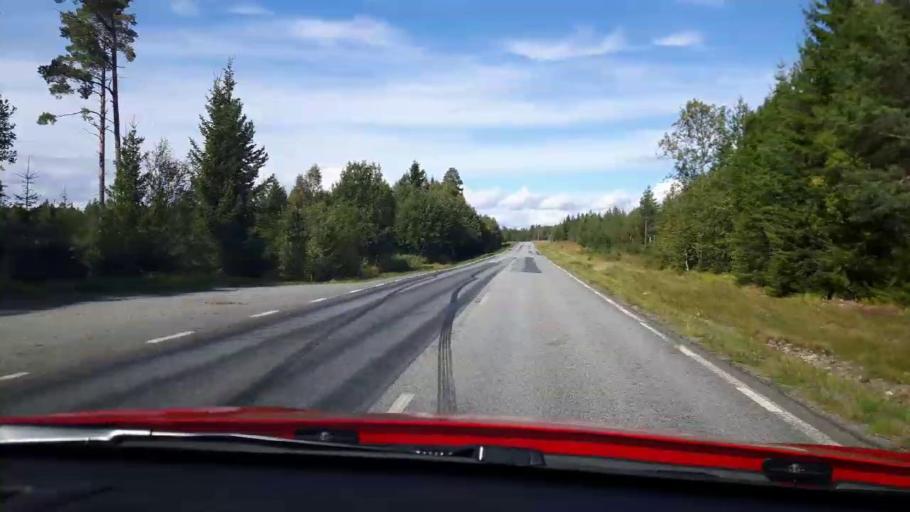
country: SE
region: Jaemtland
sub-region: OEstersunds Kommun
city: Ostersund
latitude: 63.0742
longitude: 14.4445
